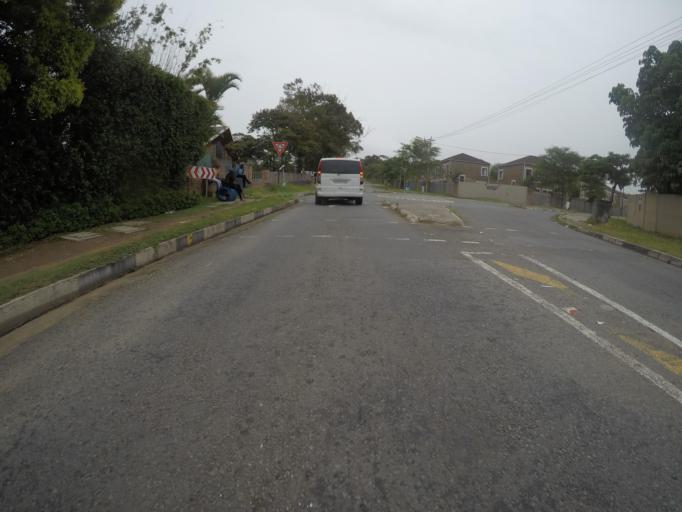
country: ZA
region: Eastern Cape
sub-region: Buffalo City Metropolitan Municipality
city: East London
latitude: -32.9617
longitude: 27.9153
